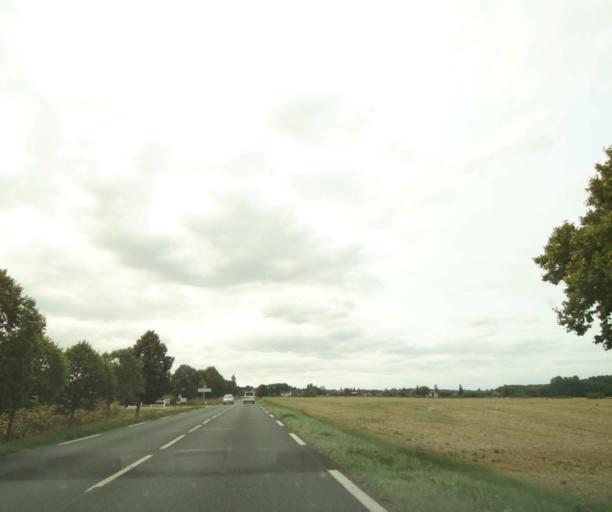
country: FR
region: Centre
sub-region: Departement d'Indre-et-Loire
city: Perrusson
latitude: 47.0835
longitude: 1.0324
